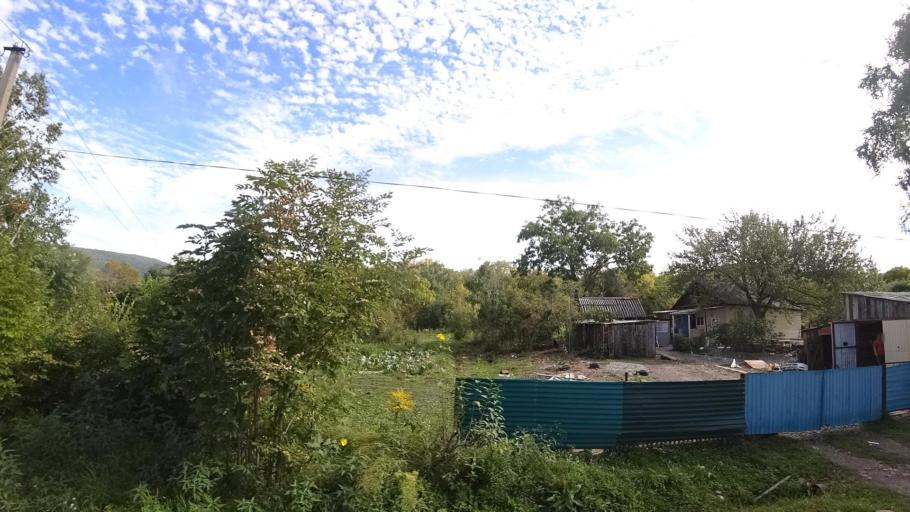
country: RU
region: Primorskiy
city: Yakovlevka
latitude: 44.3880
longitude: 133.6060
